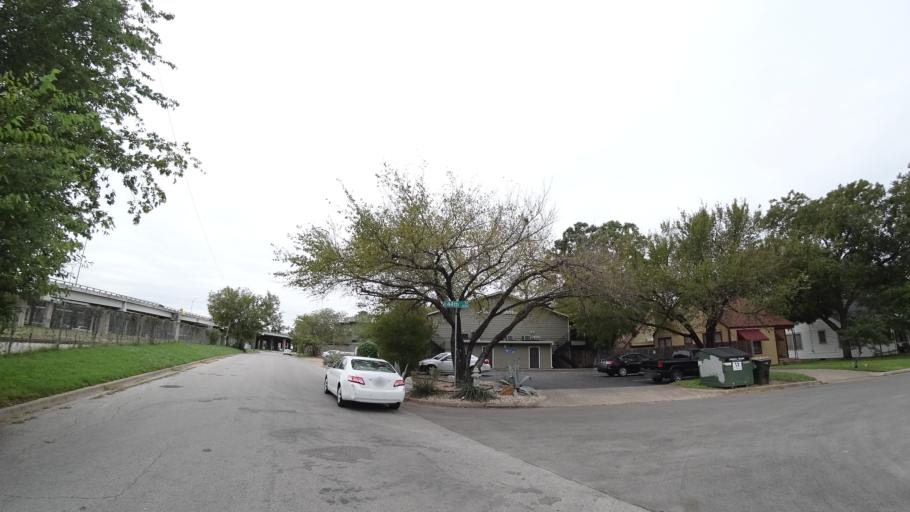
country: US
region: Texas
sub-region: Travis County
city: Austin
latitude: 30.3017
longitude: -97.7166
